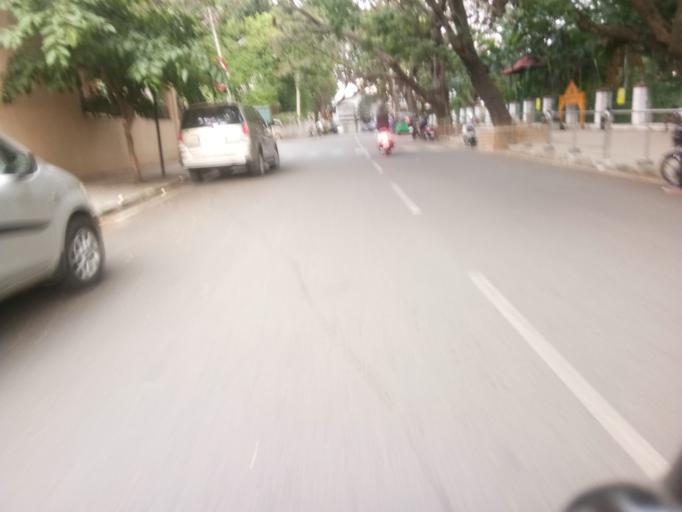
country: IN
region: Karnataka
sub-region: Bangalore Urban
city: Bangalore
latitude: 13.0046
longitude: 77.6168
